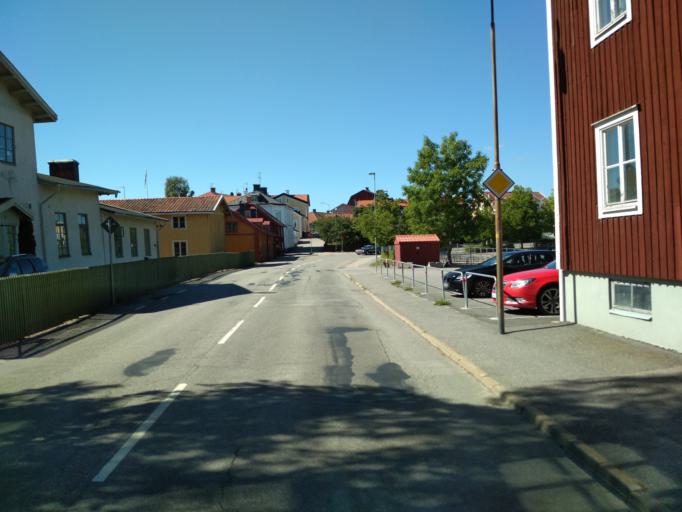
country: SE
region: Soedermanland
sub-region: Strangnas Kommun
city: Mariefred
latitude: 59.2609
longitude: 17.2267
